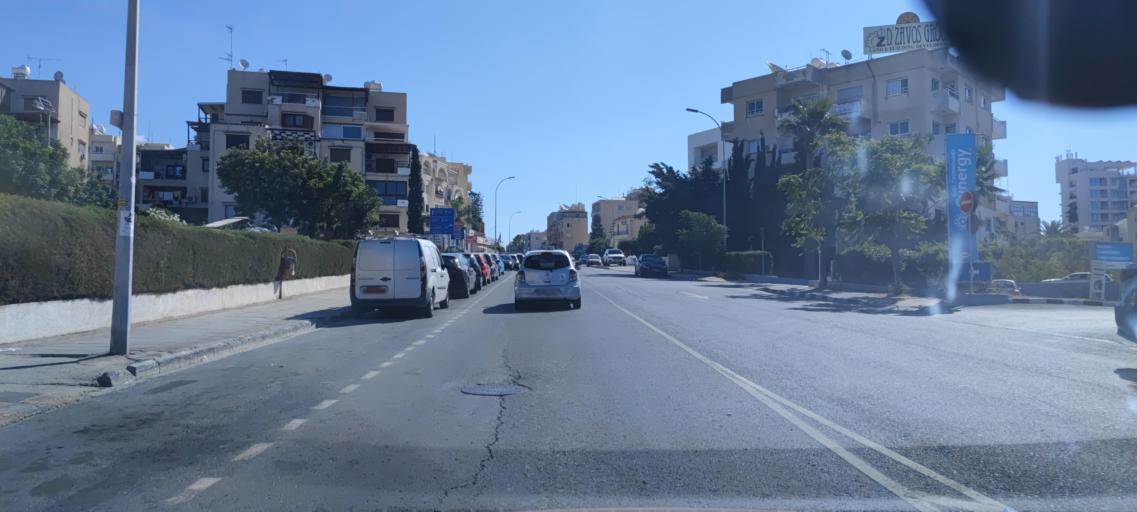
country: CY
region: Larnaka
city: Agios Tychon
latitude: 34.7088
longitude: 33.1234
